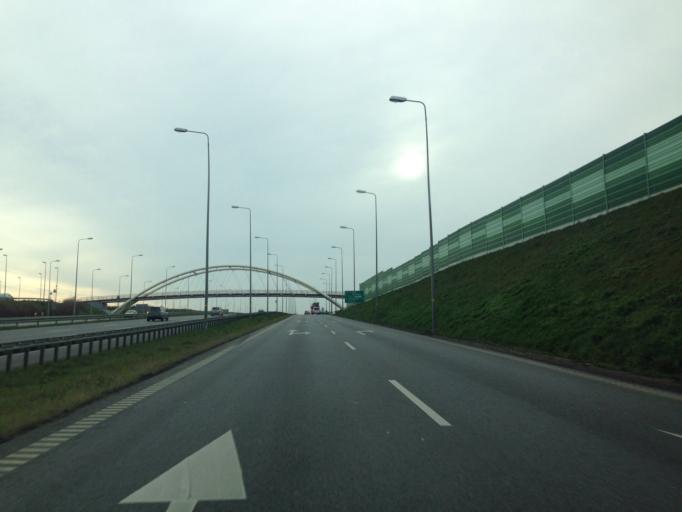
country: PL
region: Pomeranian Voivodeship
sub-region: Powiat gdanski
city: Kowale
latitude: 54.3547
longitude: 18.5185
